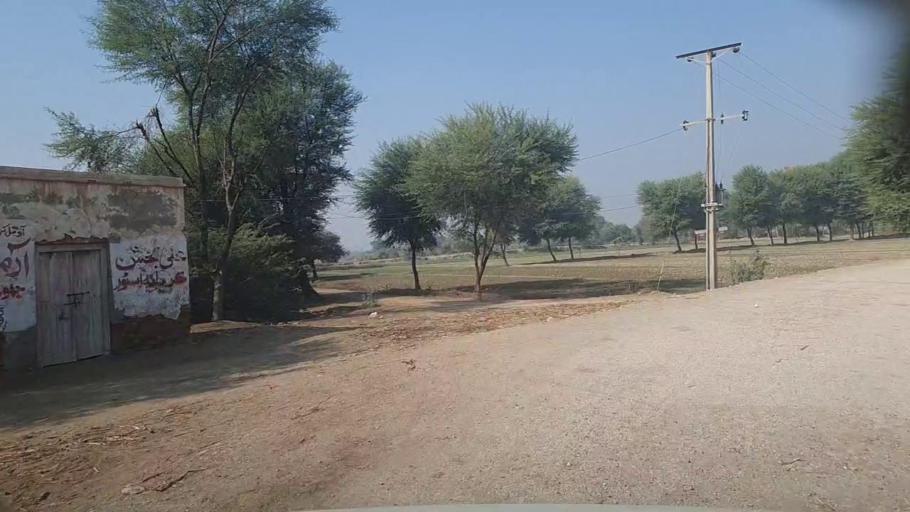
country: PK
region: Sindh
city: Kandiari
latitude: 26.9680
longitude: 68.4565
